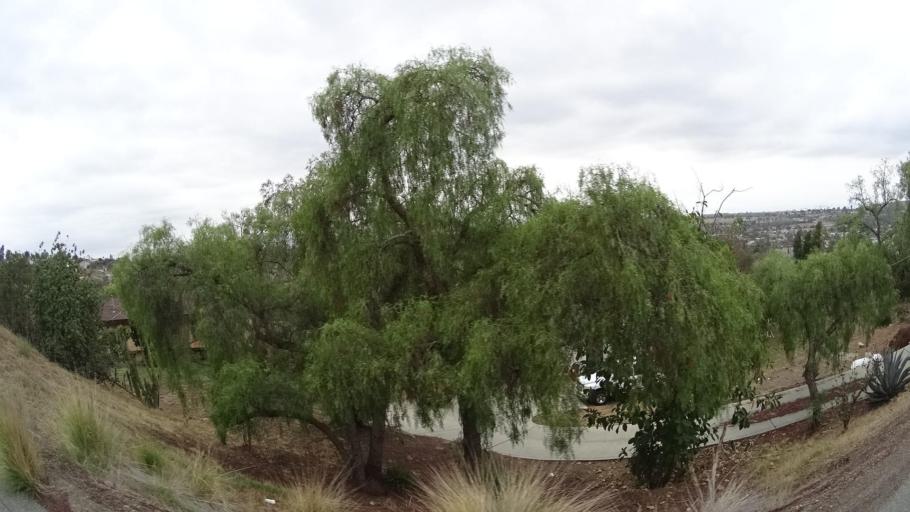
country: US
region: California
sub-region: San Diego County
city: Spring Valley
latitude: 32.7321
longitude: -117.0009
